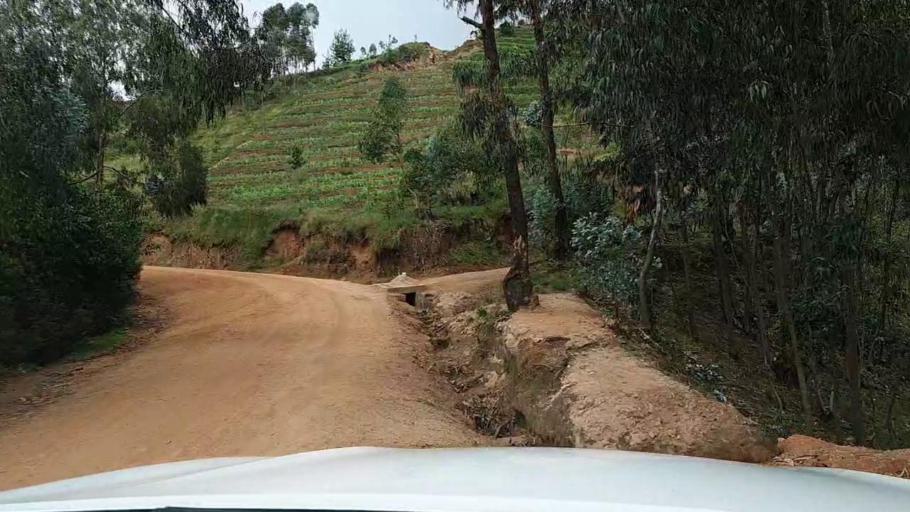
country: RW
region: Southern Province
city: Nzega
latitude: -2.4291
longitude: 29.4350
